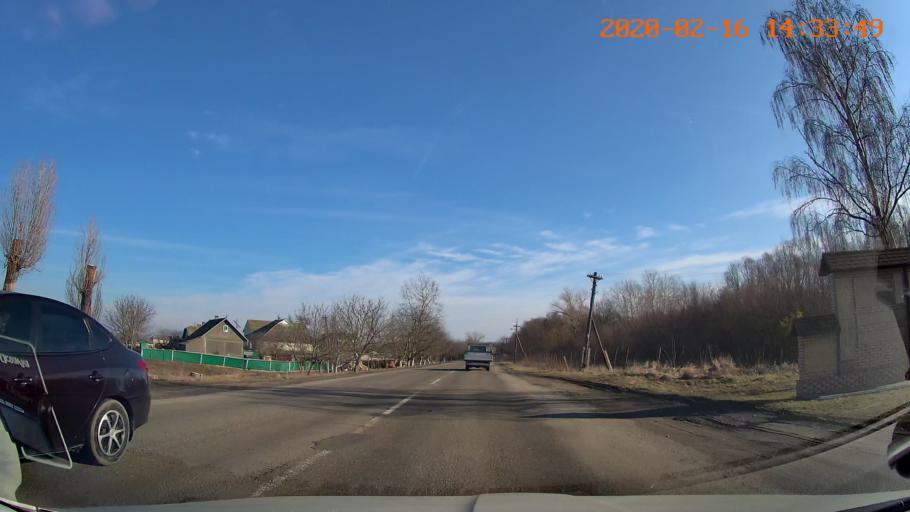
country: RO
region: Botosani
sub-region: Comuna Hudesti
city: Alba
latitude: 48.2221
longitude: 26.4694
